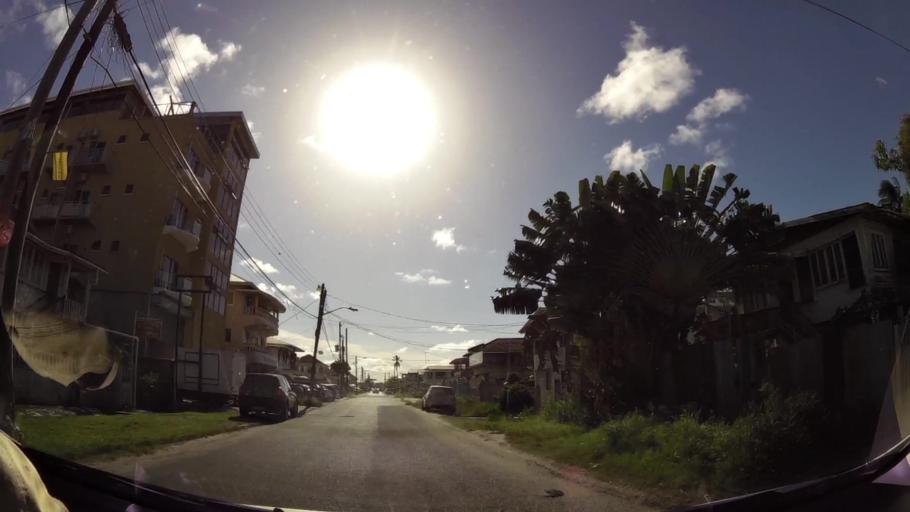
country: GY
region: Demerara-Mahaica
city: Georgetown
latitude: 6.8128
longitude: -58.1396
